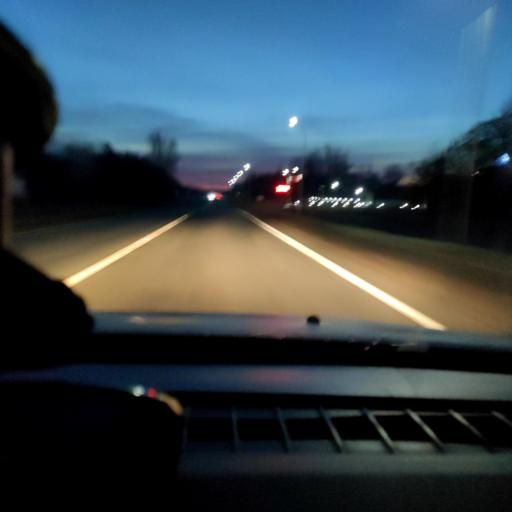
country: RU
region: Samara
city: Chapayevsk
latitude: 52.9943
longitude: 49.8170
